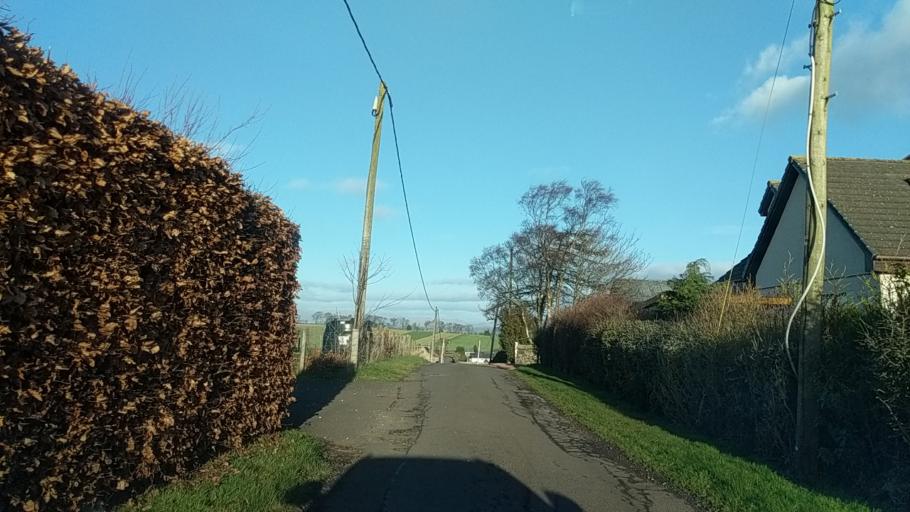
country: GB
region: Scotland
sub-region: West Lothian
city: Linlithgow
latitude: 55.9933
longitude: -3.5430
